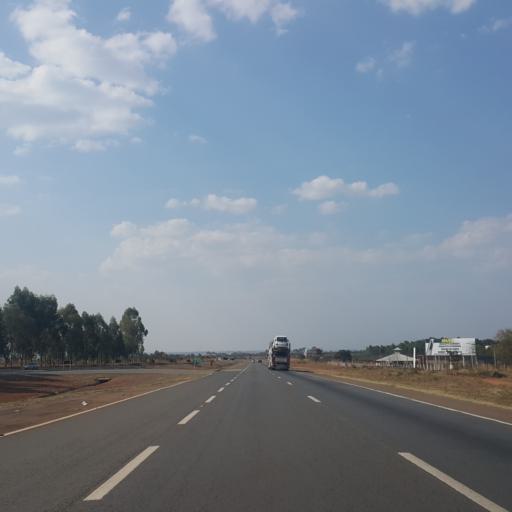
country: BR
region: Goias
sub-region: Abadiania
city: Abadiania
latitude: -16.2100
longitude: -48.7433
